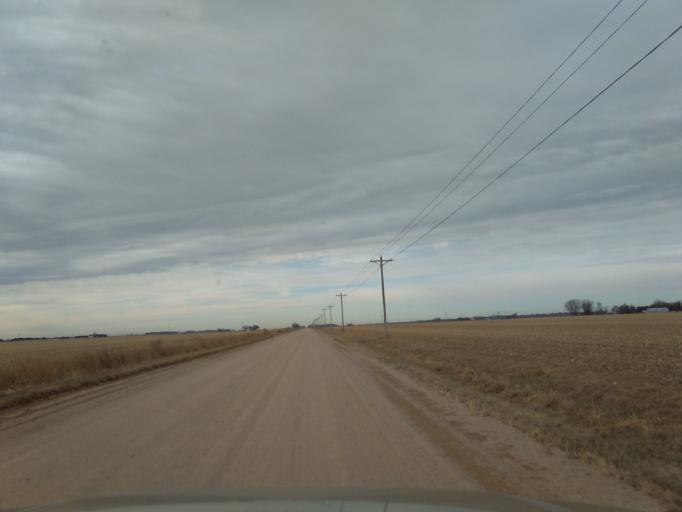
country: US
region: Nebraska
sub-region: Buffalo County
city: Gibbon
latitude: 40.6408
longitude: -98.9053
